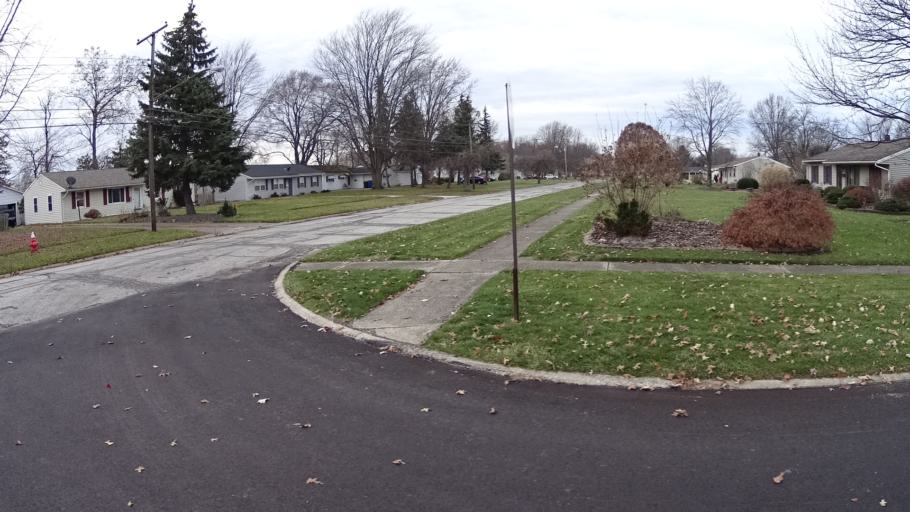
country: US
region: Ohio
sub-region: Lorain County
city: North Ridgeville
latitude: 41.3828
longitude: -81.9965
